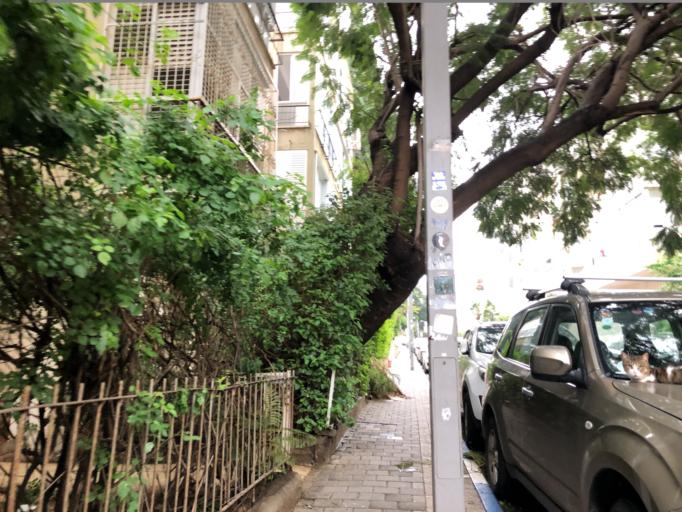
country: IL
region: Tel Aviv
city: Tel Aviv
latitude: 32.0716
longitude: 34.7751
